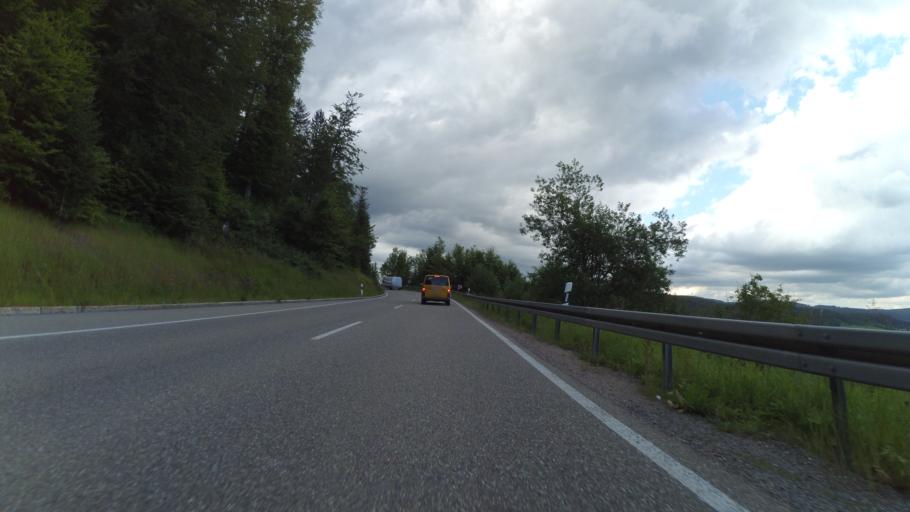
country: DE
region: Baden-Wuerttemberg
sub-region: Freiburg Region
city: Hinterzarten
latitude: 47.8807
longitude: 8.1251
